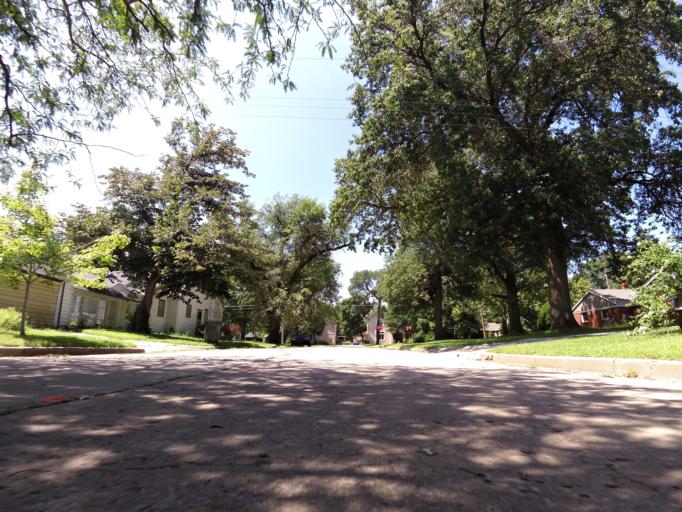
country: US
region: Kansas
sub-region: Sedgwick County
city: Wichita
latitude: 37.7001
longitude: -97.2928
